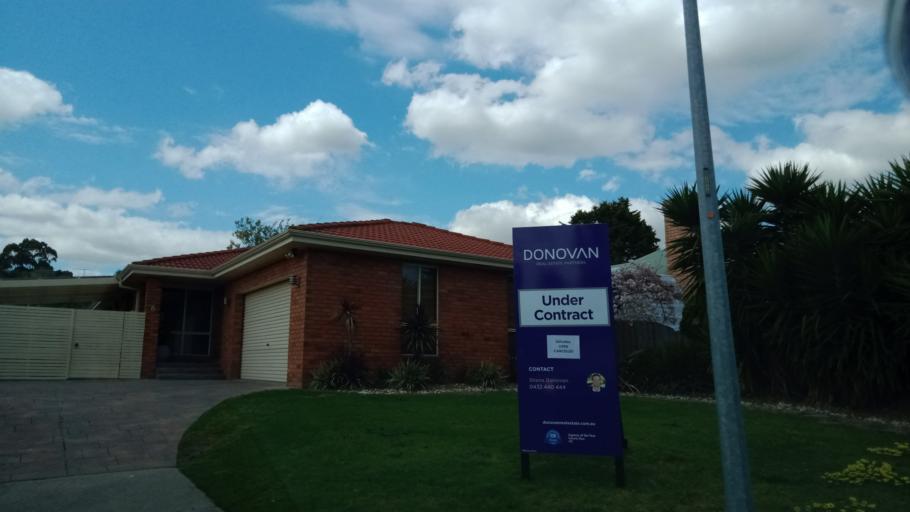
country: AU
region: Victoria
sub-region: Frankston
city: Carrum Downs
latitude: -38.0908
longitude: 145.1886
